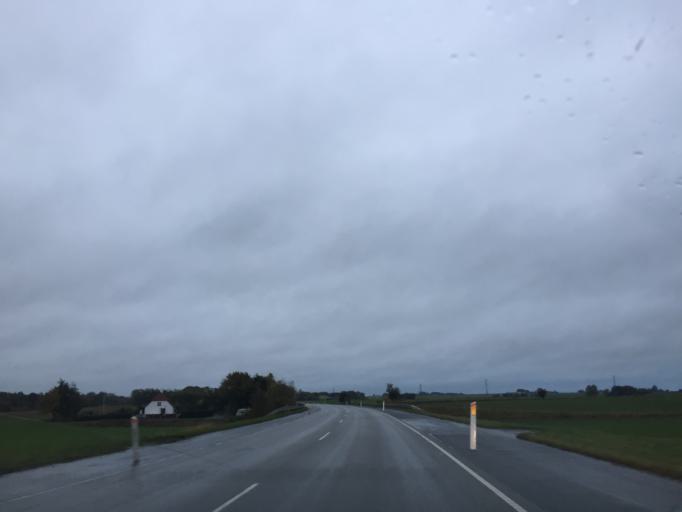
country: DK
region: Zealand
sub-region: Ringsted Kommune
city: Ringsted
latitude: 55.4744
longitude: 11.7401
